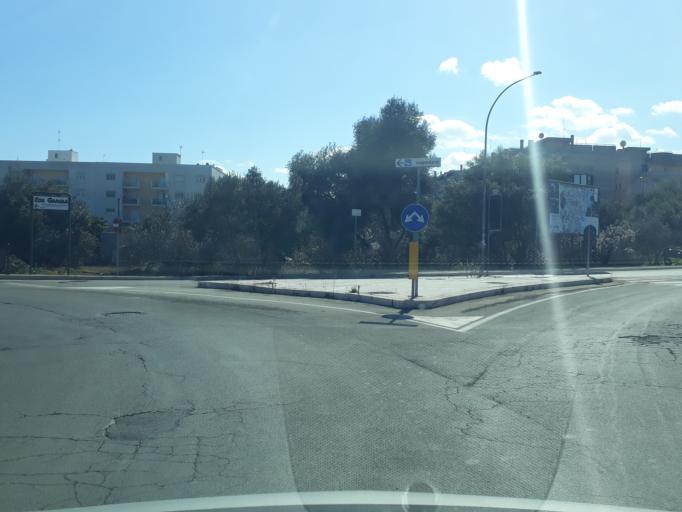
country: IT
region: Apulia
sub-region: Provincia di Bari
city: Monopoli
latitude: 40.9521
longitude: 17.2858
